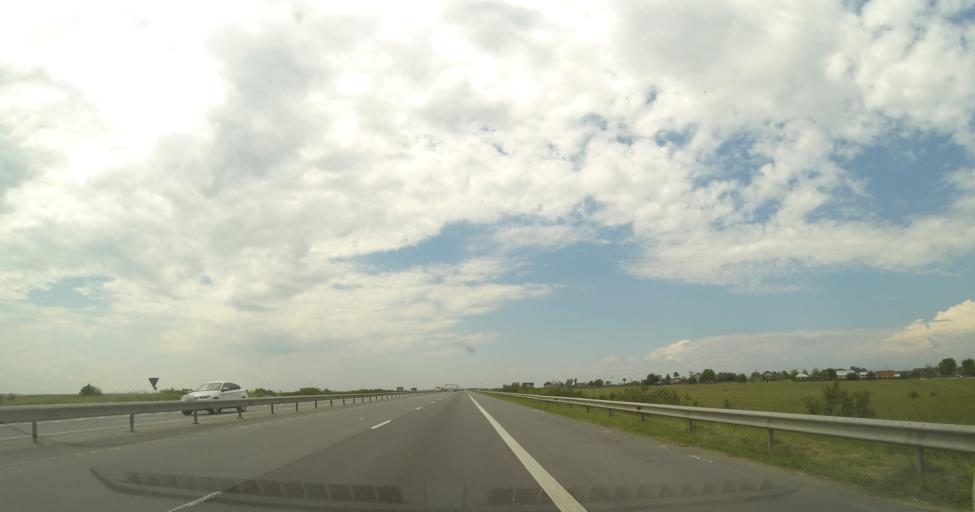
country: RO
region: Dambovita
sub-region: Comuna Petresti
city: Greci
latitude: 44.6568
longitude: 25.3384
